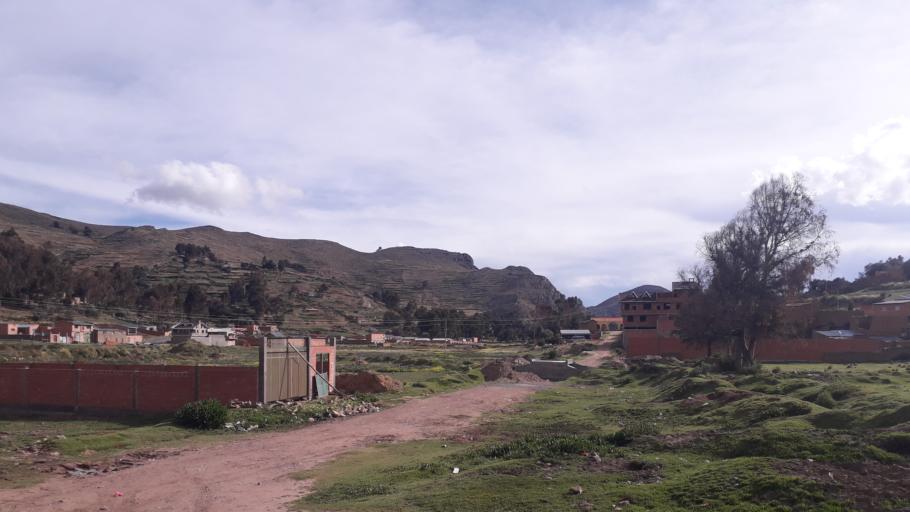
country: PE
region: Puno
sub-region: Moho
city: Putina
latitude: -15.5358
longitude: -69.2521
